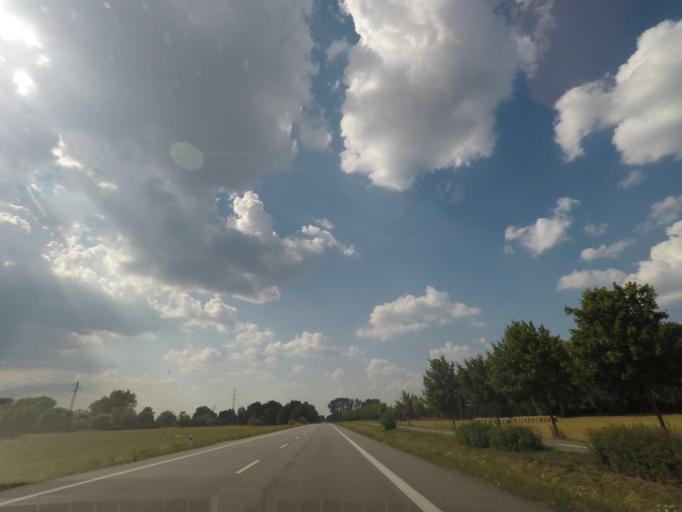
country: CZ
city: Albrechtice nad Orlici
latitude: 50.1625
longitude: 16.0548
